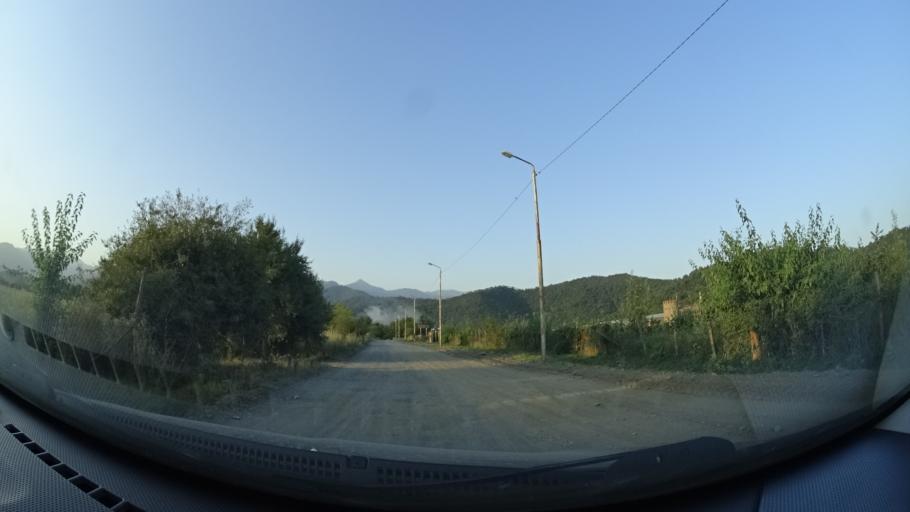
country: GE
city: Bagdadi
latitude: 41.8656
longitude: 46.0179
